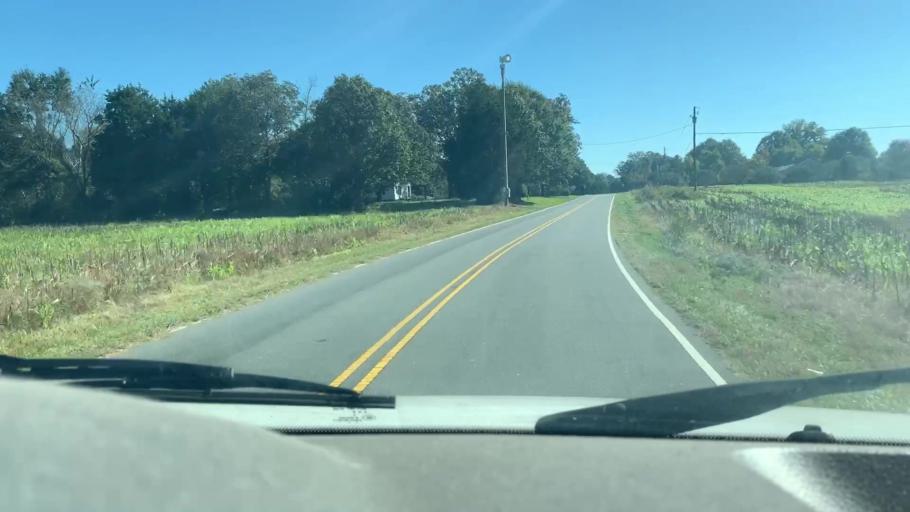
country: US
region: North Carolina
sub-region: Mecklenburg County
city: Cornelius
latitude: 35.4549
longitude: -80.8333
